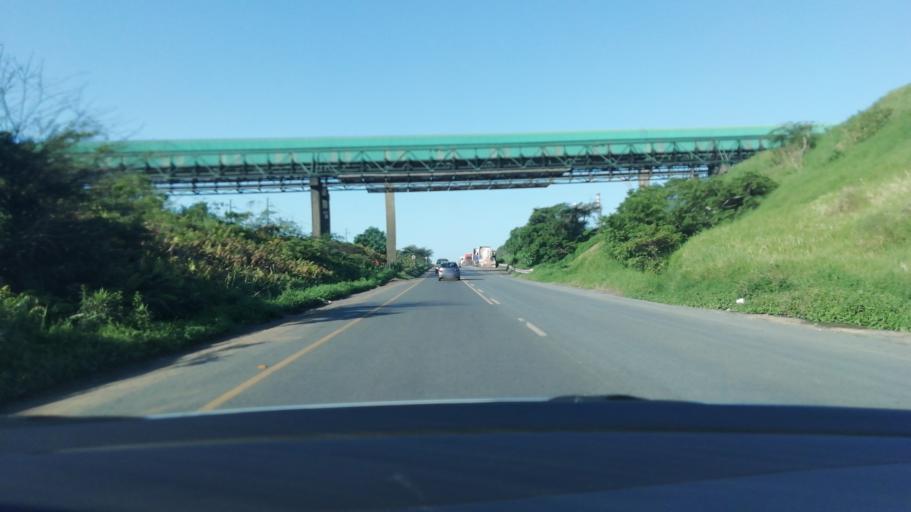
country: ZA
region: KwaZulu-Natal
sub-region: uThungulu District Municipality
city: Richards Bay
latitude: -28.7786
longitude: 32.0298
